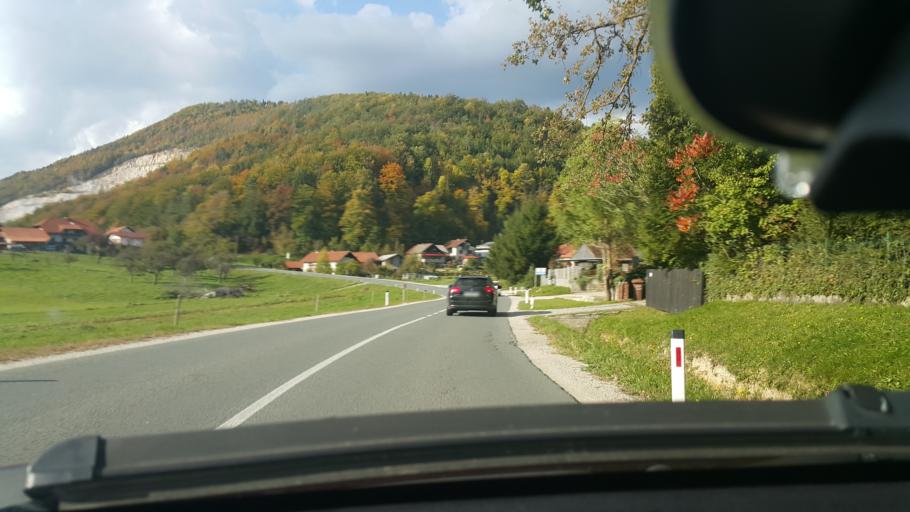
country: SI
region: Zrece
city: Zrece
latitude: 46.3616
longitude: 15.3681
